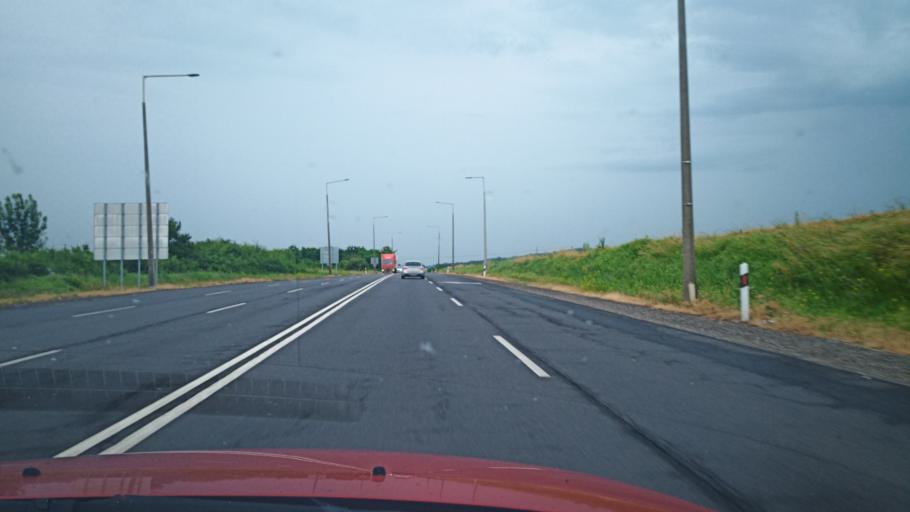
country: HU
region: Borsod-Abauj-Zemplen
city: Malyi
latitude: 48.0505
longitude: 20.7997
